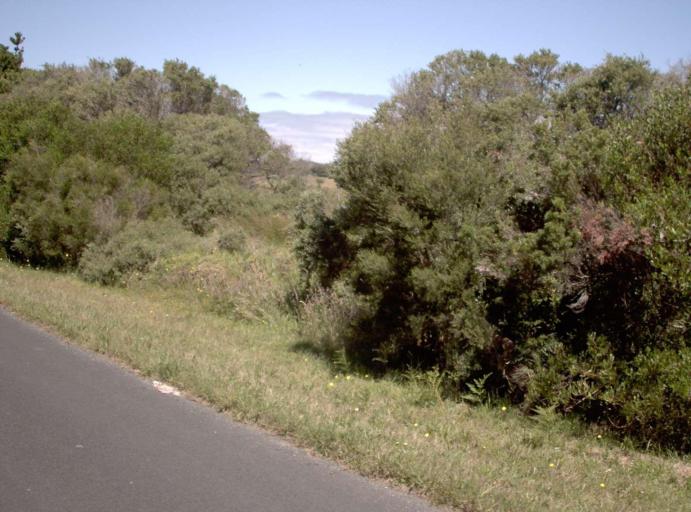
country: AU
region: Victoria
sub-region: Bass Coast
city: North Wonthaggi
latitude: -38.8179
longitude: 146.1124
